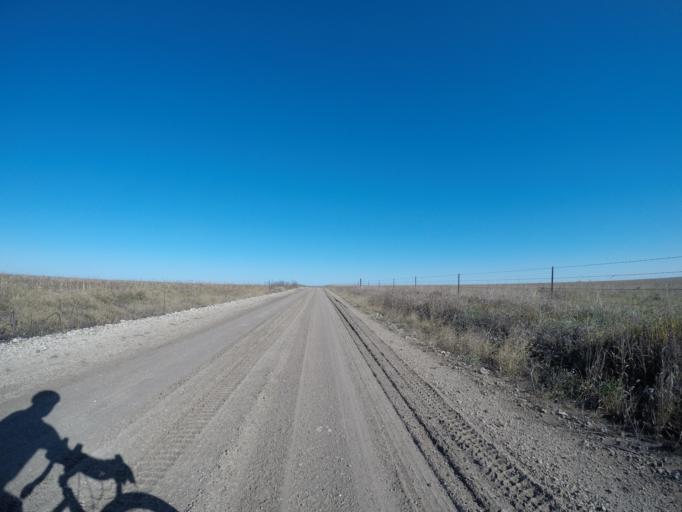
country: US
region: Kansas
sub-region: Wabaunsee County
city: Alma
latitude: 38.8807
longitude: -96.4096
